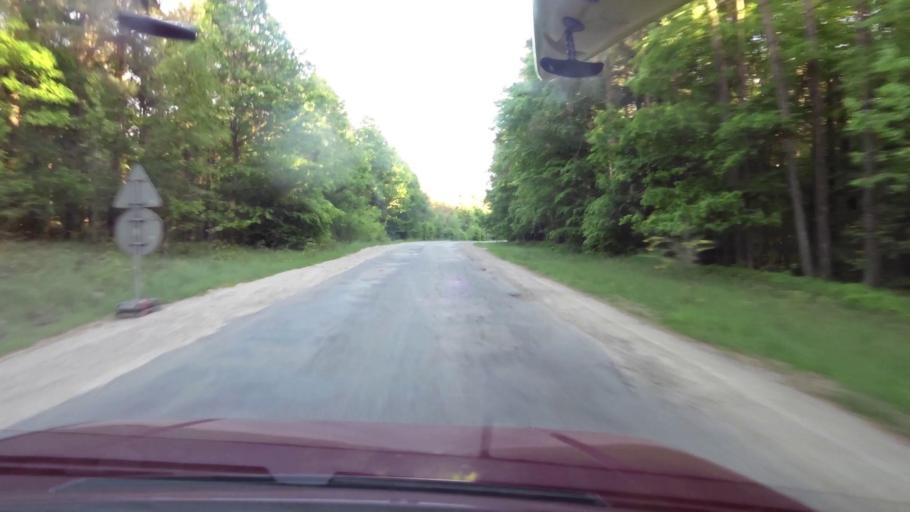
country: PL
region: West Pomeranian Voivodeship
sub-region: Powiat szczecinecki
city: Bialy Bor
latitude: 53.9258
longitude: 16.8033
